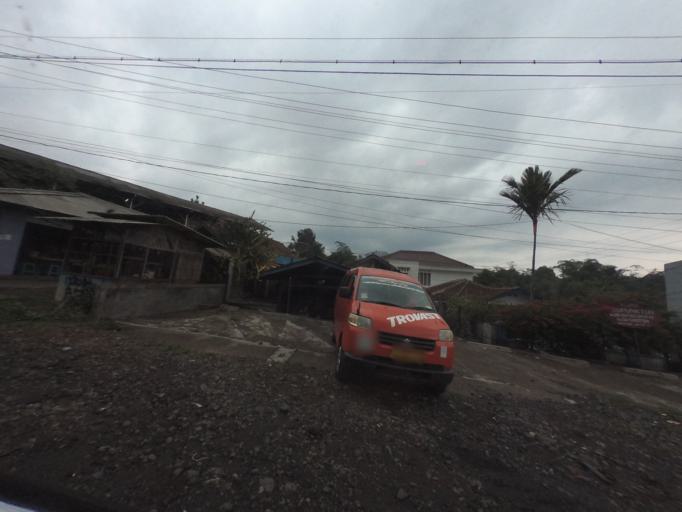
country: ID
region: West Java
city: Cicurug
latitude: -6.8418
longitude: 106.7617
